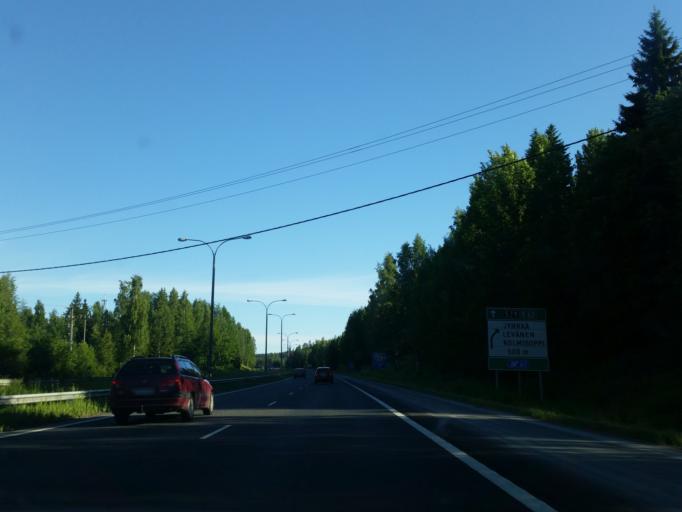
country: FI
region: Northern Savo
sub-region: Kuopio
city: Kuopio
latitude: 62.8717
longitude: 27.6200
